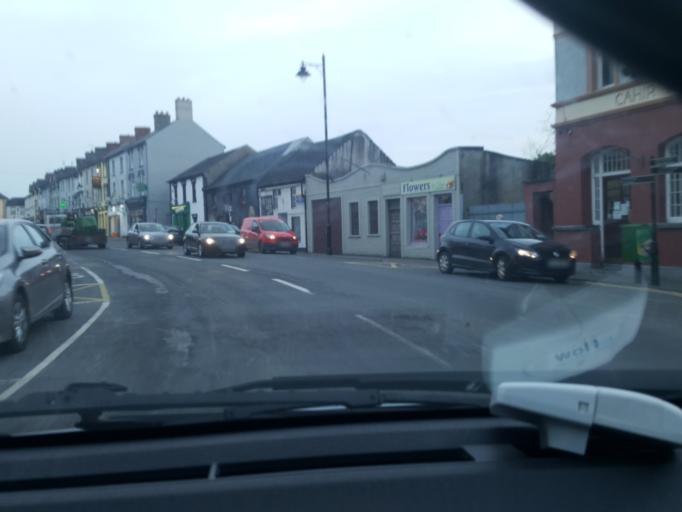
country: IE
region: Munster
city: Cahir
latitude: 52.3762
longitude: -7.9245
